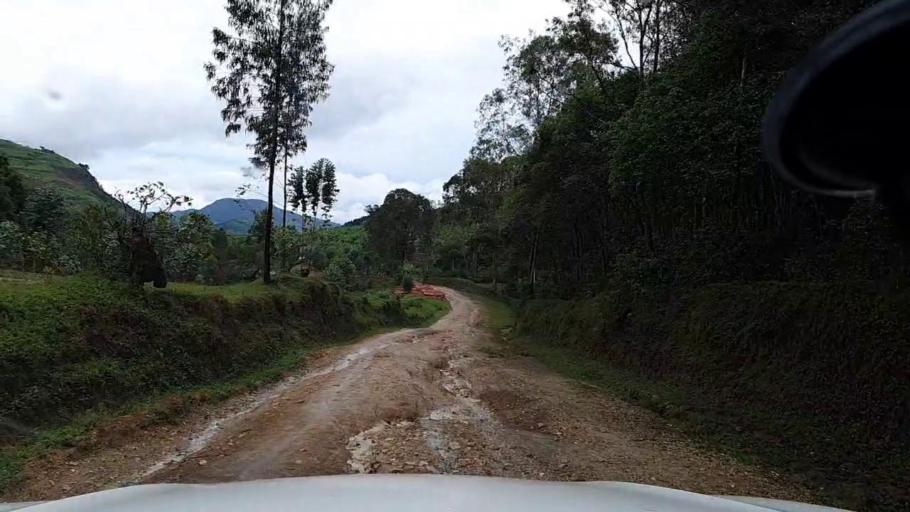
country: RW
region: Western Province
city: Kibuye
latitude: -2.1182
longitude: 29.4929
